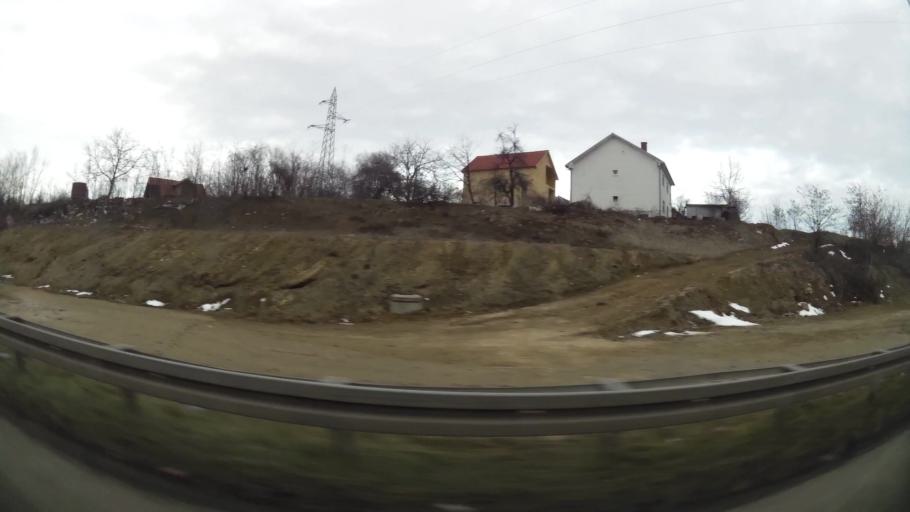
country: RS
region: Central Serbia
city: Sremcica
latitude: 44.7118
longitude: 20.3660
